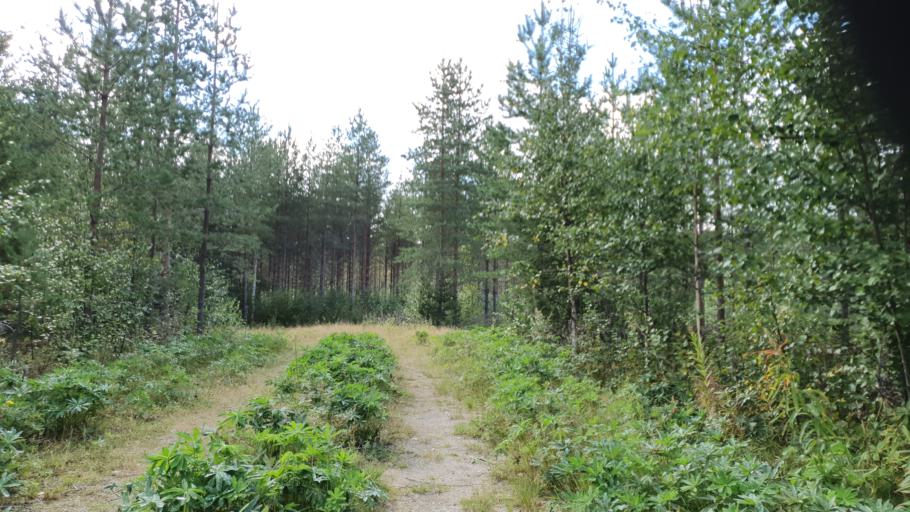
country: FI
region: Kainuu
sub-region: Kehys-Kainuu
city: Kuhmo
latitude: 64.1460
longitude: 29.3542
